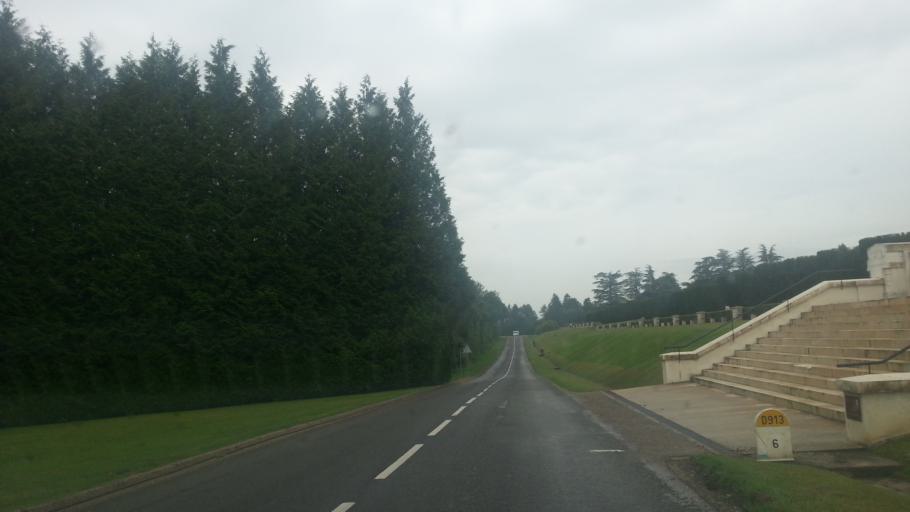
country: FR
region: Lorraine
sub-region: Departement de la Meuse
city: Verdun
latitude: 49.2064
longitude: 5.4259
